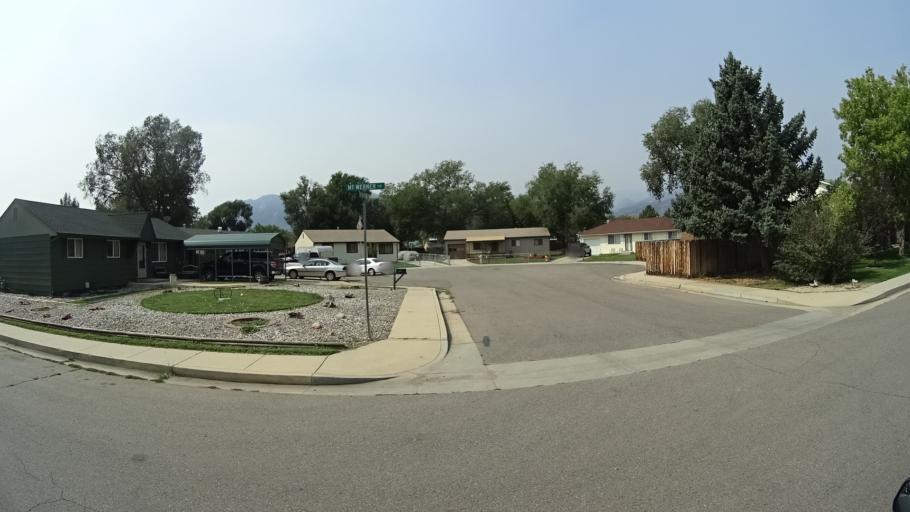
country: US
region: Colorado
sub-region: El Paso County
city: Colorado Springs
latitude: 38.8025
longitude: -104.8083
